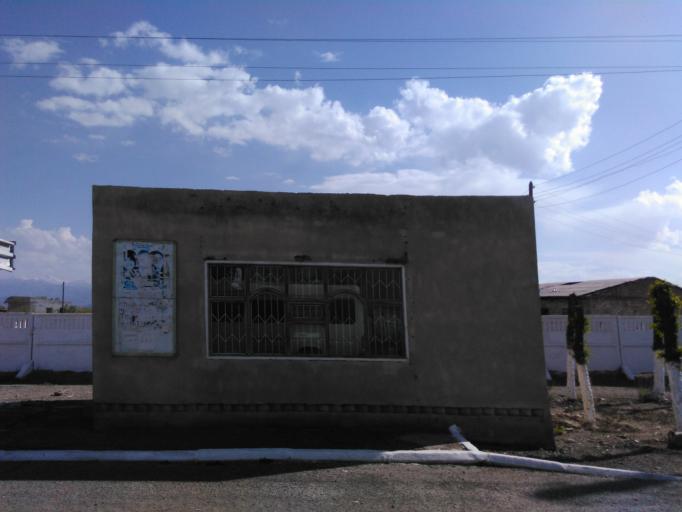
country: KG
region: Ysyk-Koel
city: Balykchy
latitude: 42.4526
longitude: 76.1653
